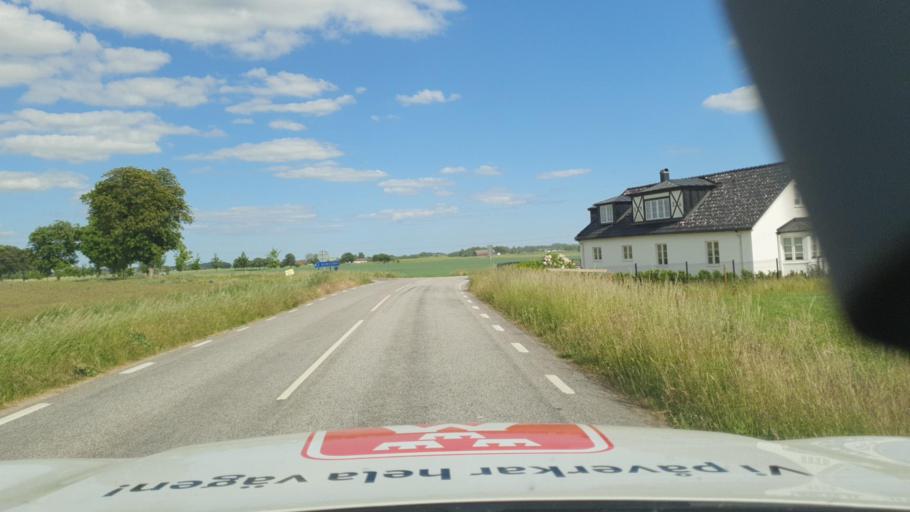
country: SE
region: Skane
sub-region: Ystads Kommun
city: Kopingebro
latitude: 55.4746
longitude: 13.9032
